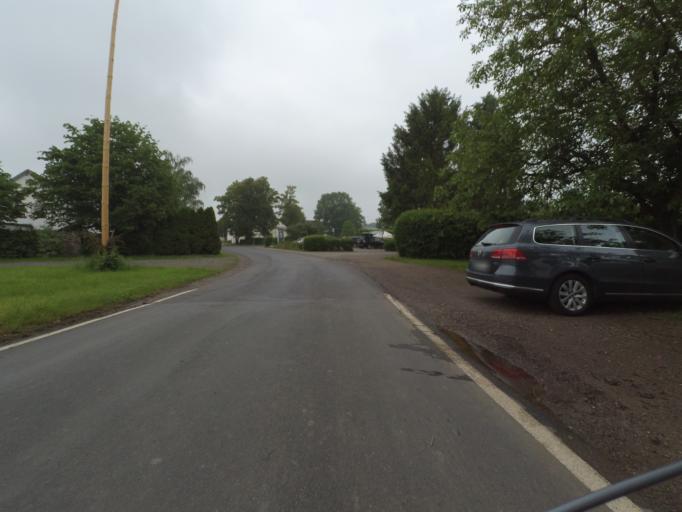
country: DE
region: Rheinland-Pfalz
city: Valwig
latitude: 50.1501
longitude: 7.2238
